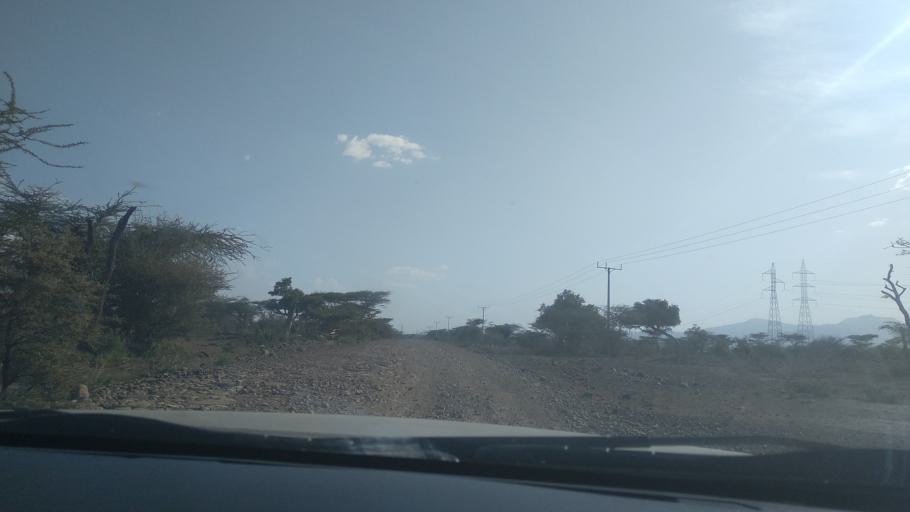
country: ET
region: Oromiya
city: Hirna
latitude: 9.4951
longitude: 41.0298
